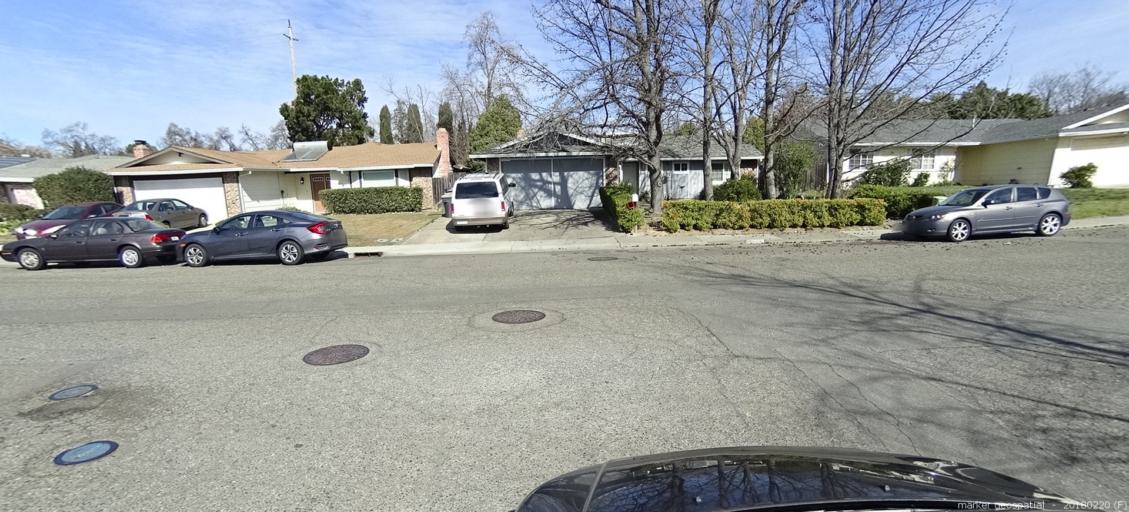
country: US
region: California
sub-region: Sacramento County
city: Orangevale
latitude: 38.6724
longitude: -121.2194
